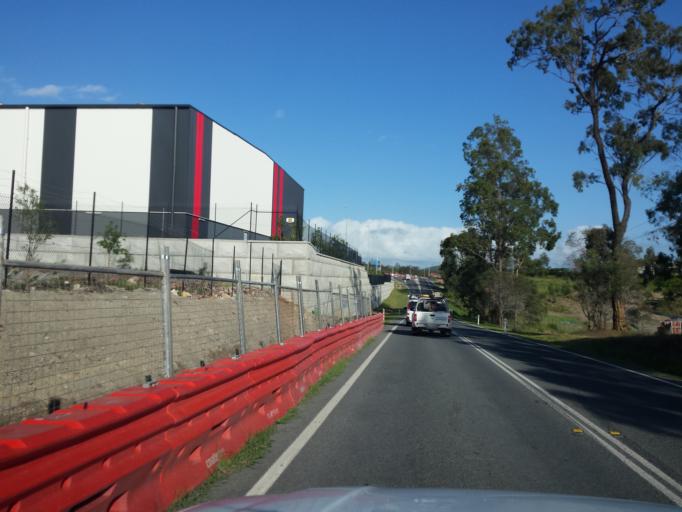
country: AU
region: Queensland
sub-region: Logan
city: Windaroo
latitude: -27.7656
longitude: 153.2177
